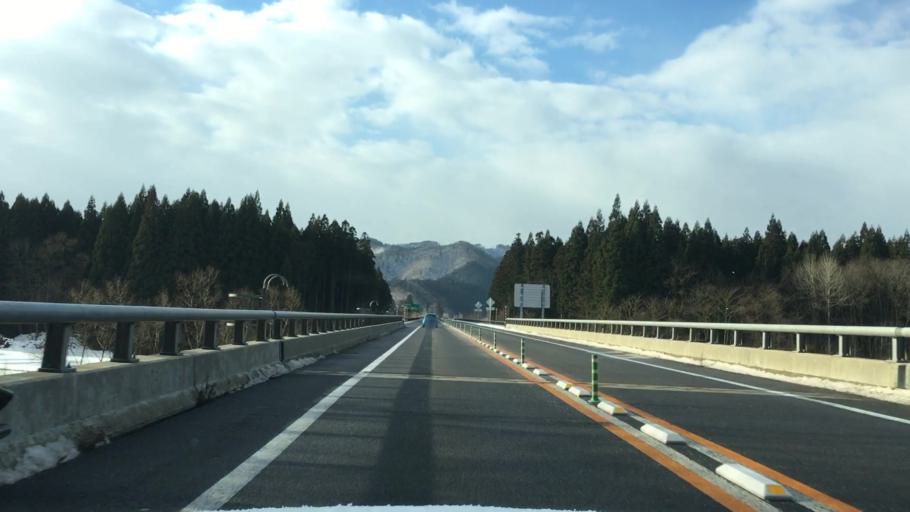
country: JP
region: Akita
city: Odate
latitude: 40.2424
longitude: 140.5078
